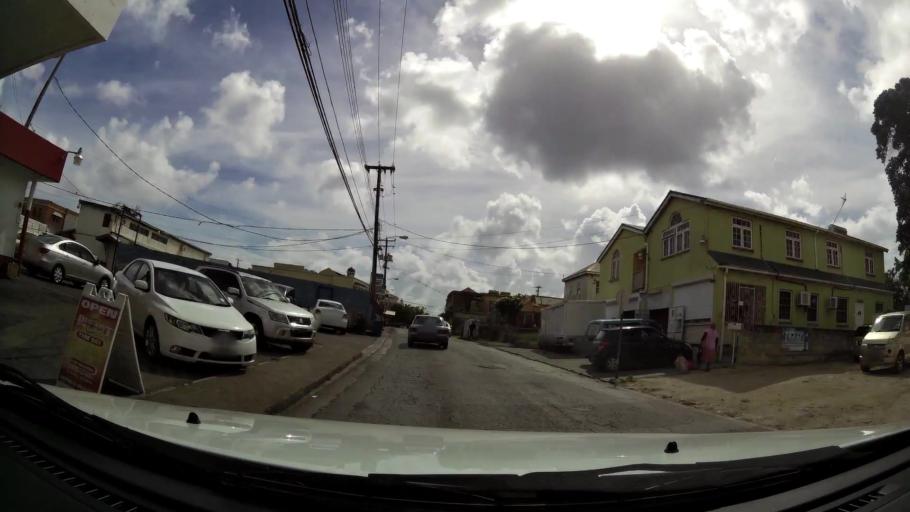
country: BB
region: Saint Michael
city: Bridgetown
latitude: 13.1039
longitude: -59.6138
